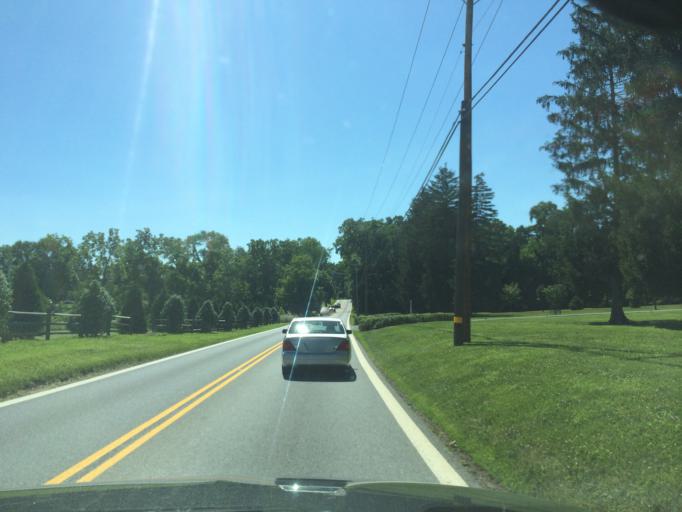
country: US
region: Maryland
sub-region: Baltimore County
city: Pikesville
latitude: 39.4123
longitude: -76.7213
